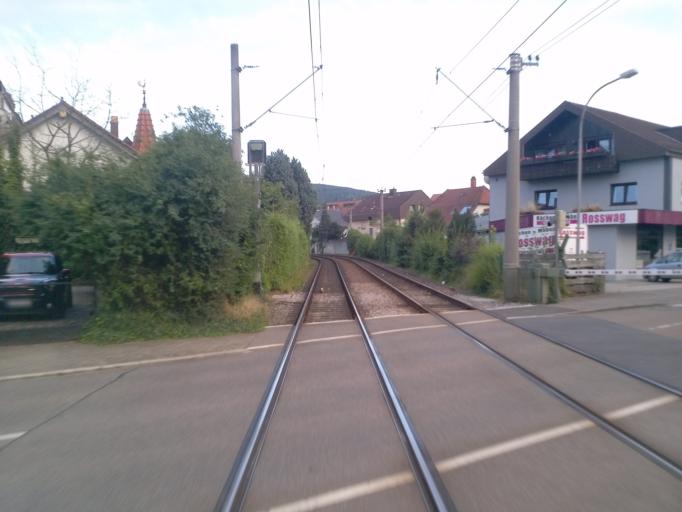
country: DE
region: Baden-Wuerttemberg
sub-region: Karlsruhe Region
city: Ettlingen
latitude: 48.9449
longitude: 8.3990
